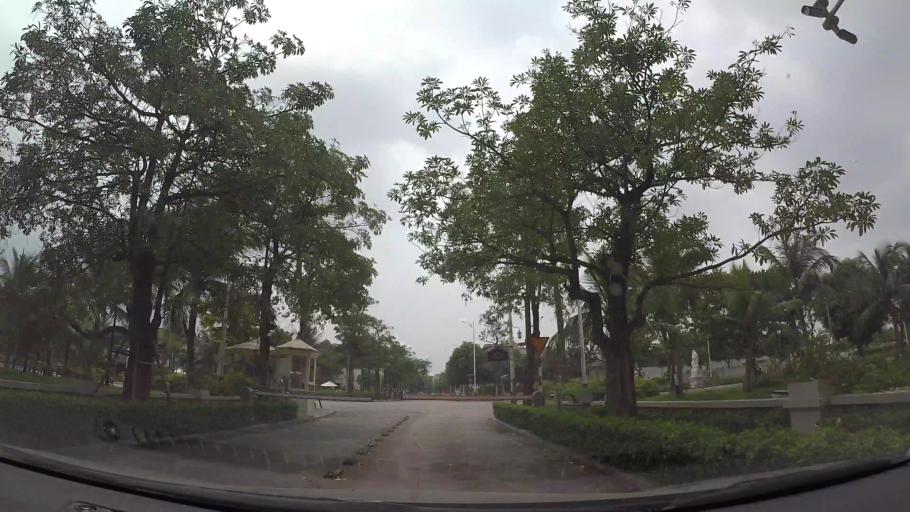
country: VN
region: Ha Noi
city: Trau Quy
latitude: 21.0442
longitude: 105.9149
